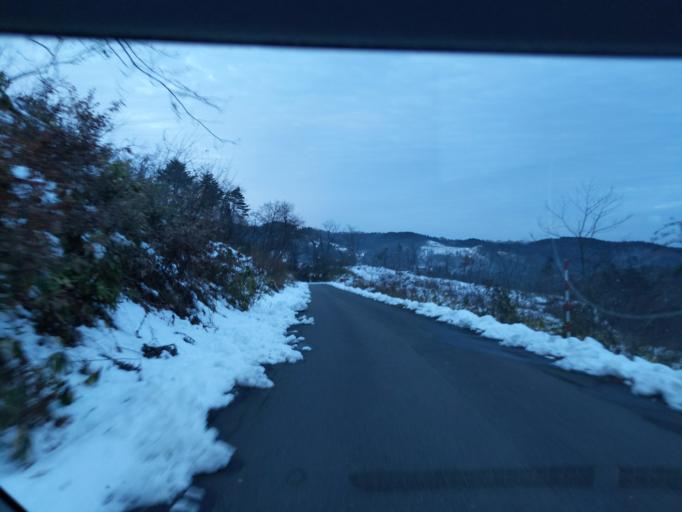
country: JP
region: Iwate
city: Mizusawa
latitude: 39.0539
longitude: 141.0318
